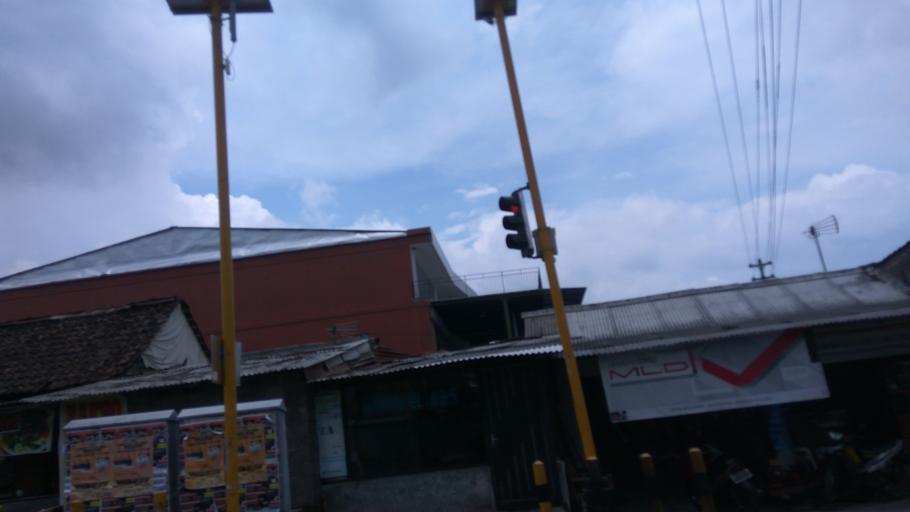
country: ID
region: Daerah Istimewa Yogyakarta
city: Melati
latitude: -7.7265
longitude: 110.3997
